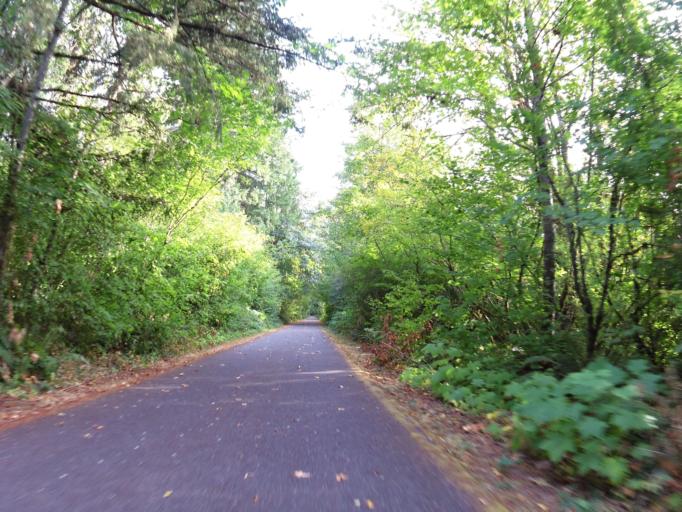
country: US
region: Washington
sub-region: Thurston County
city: Lacey
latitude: 46.9753
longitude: -122.8128
